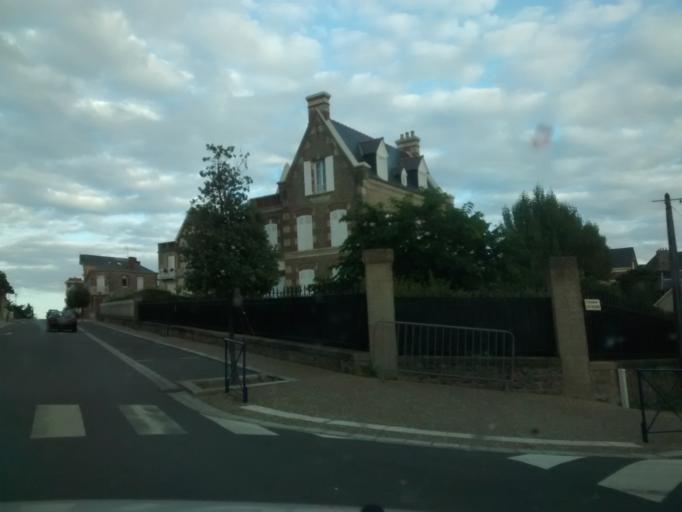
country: FR
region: Brittany
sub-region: Departement d'Ille-et-Vilaine
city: Saint-Lunaire
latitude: 48.6376
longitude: -2.1147
